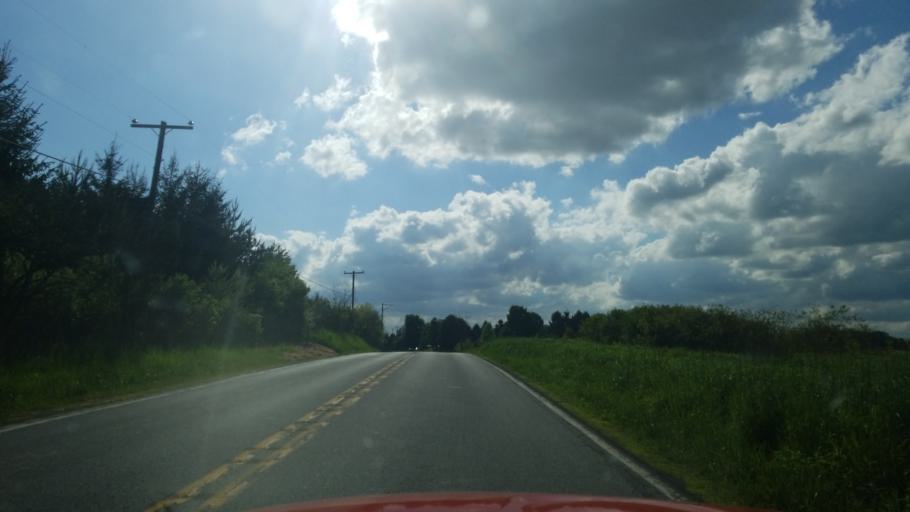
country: US
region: Pennsylvania
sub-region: Clearfield County
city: Hyde
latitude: 40.9752
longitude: -78.4504
